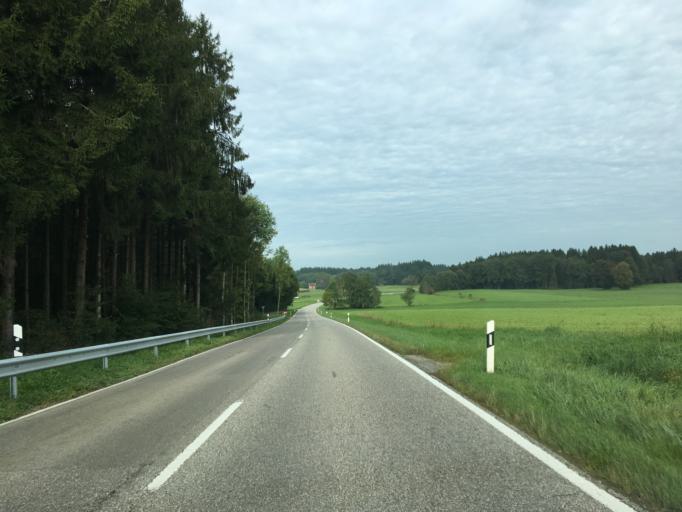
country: DE
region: Bavaria
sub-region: Upper Bavaria
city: Schonstett
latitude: 47.9933
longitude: 12.2596
